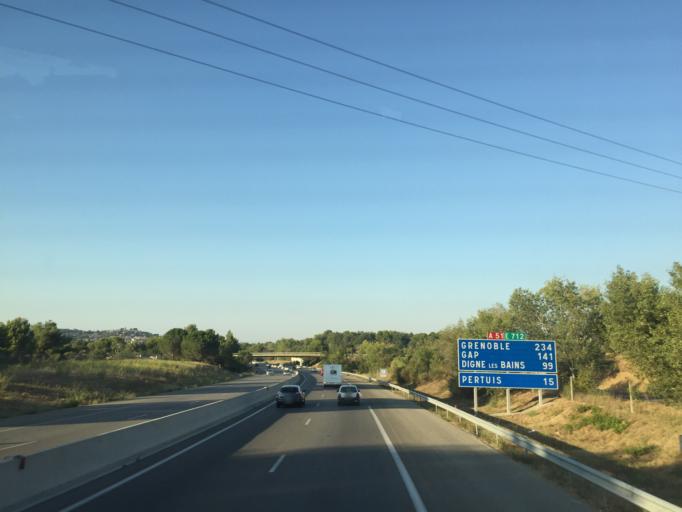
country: FR
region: Provence-Alpes-Cote d'Azur
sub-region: Departement des Bouches-du-Rhone
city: Venelles
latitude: 43.5766
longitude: 5.4731
